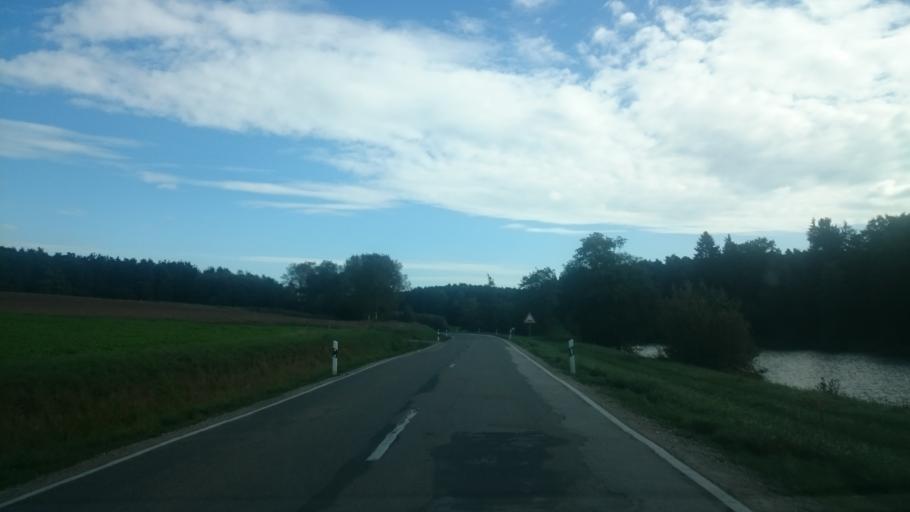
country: DE
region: Bavaria
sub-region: Regierungsbezirk Mittelfranken
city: Hilpoltstein
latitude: 49.1498
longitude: 11.2277
